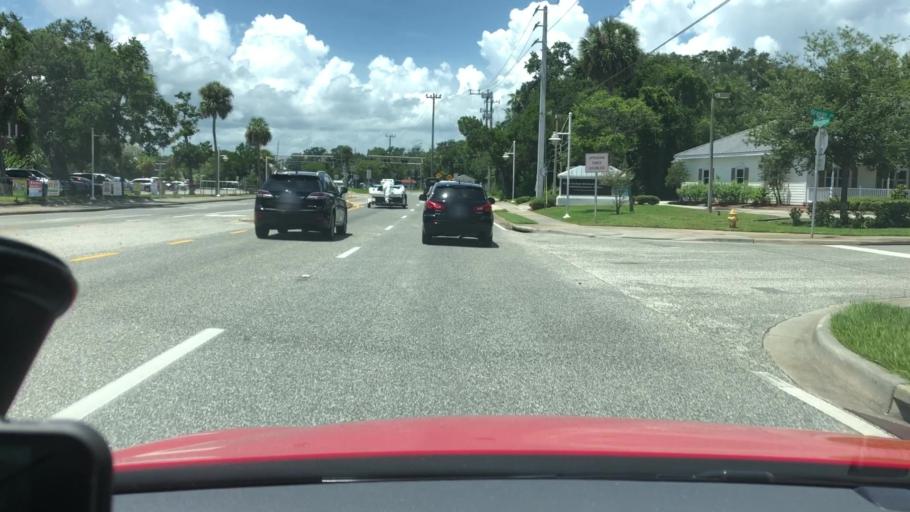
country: US
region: Florida
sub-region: Volusia County
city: South Daytona
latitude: 29.1610
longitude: -81.0185
